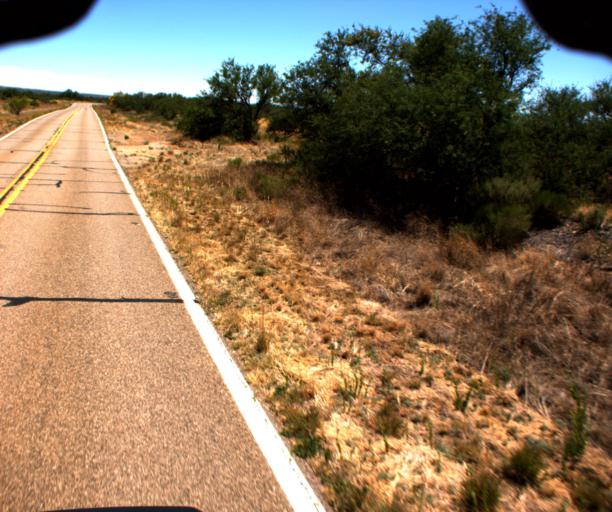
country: US
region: Arizona
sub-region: Pima County
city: Arivaca Junction
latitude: 31.6694
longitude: -111.4878
